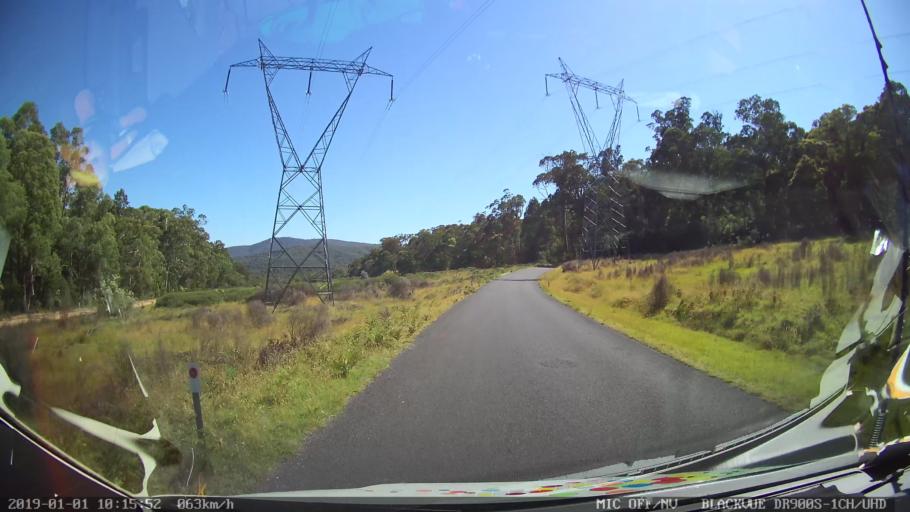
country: AU
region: New South Wales
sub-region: Snowy River
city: Jindabyne
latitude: -36.0975
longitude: 148.1626
